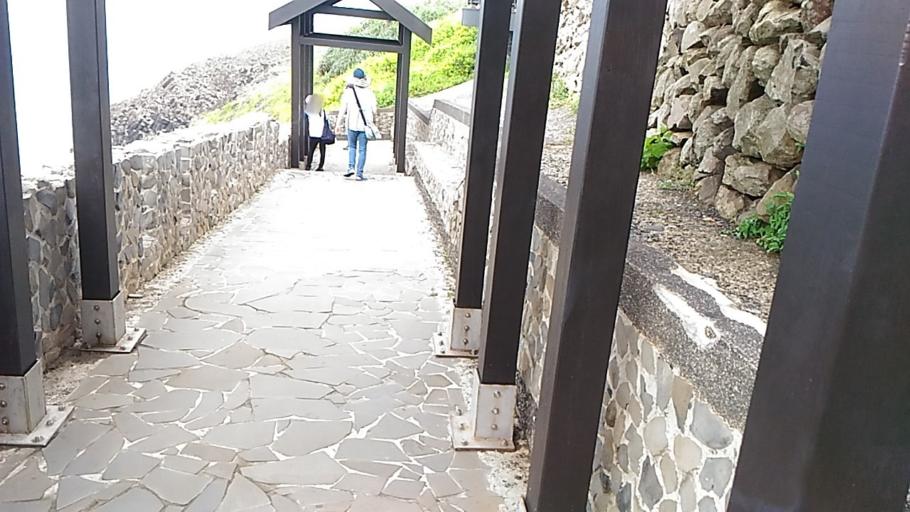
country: TW
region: Taiwan
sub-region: Penghu
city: Ma-kung
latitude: 23.2021
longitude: 119.4353
